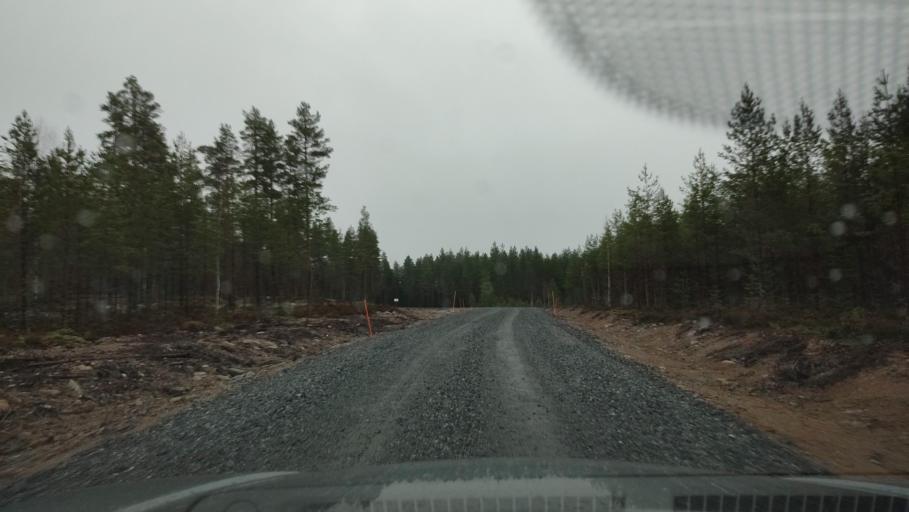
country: FI
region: Southern Ostrobothnia
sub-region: Suupohja
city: Karijoki
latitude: 62.1487
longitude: 21.6154
